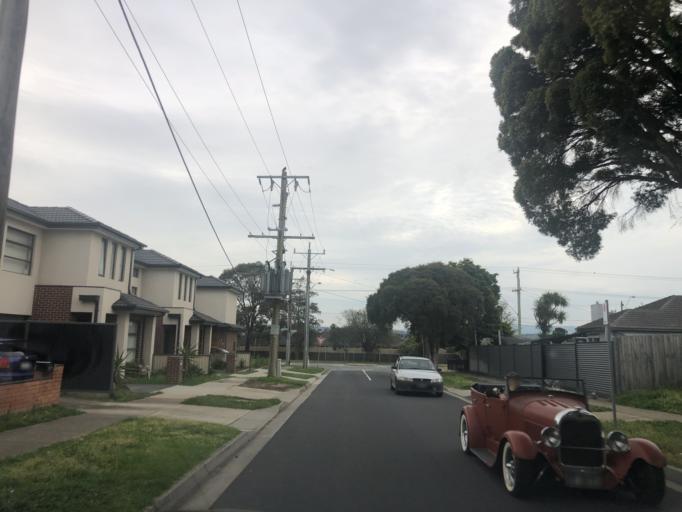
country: AU
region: Victoria
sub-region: Casey
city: Hallam
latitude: -38.0013
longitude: 145.2658
